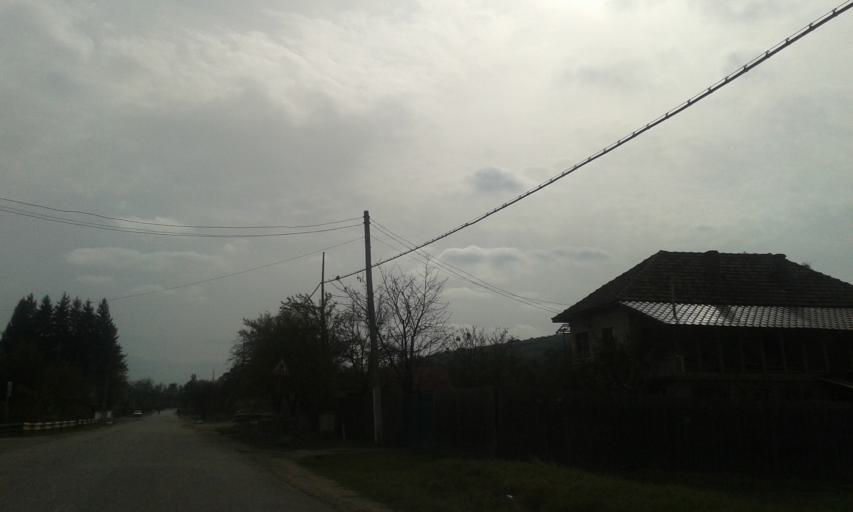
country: RO
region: Gorj
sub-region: Comuna Licuriciu
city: Licuriciu
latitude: 44.8818
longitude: 23.6312
